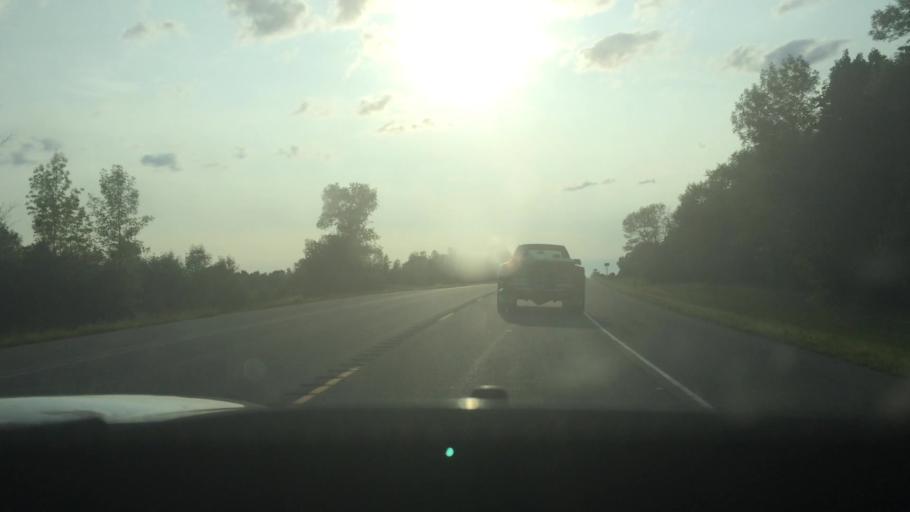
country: US
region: New York
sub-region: St. Lawrence County
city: Ogdensburg
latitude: 44.6788
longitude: -75.5050
